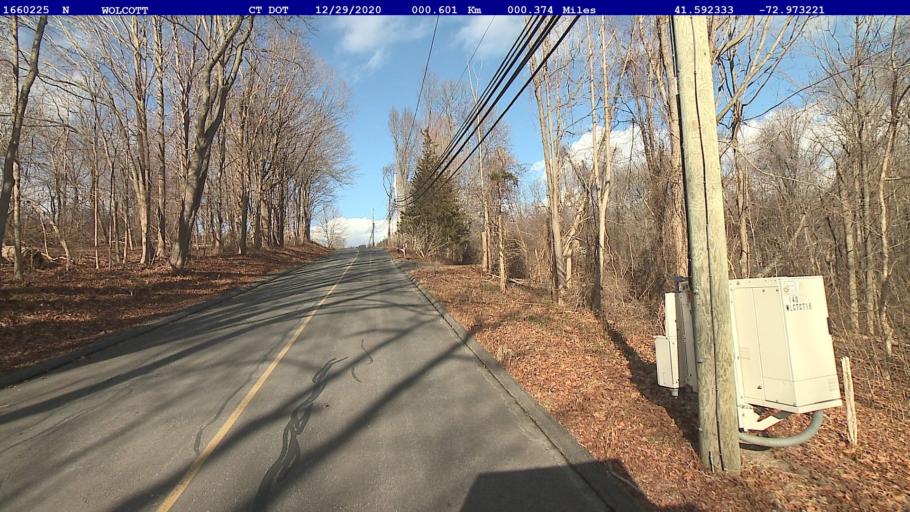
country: US
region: Connecticut
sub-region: New Haven County
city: Wolcott
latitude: 41.5923
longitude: -72.9732
